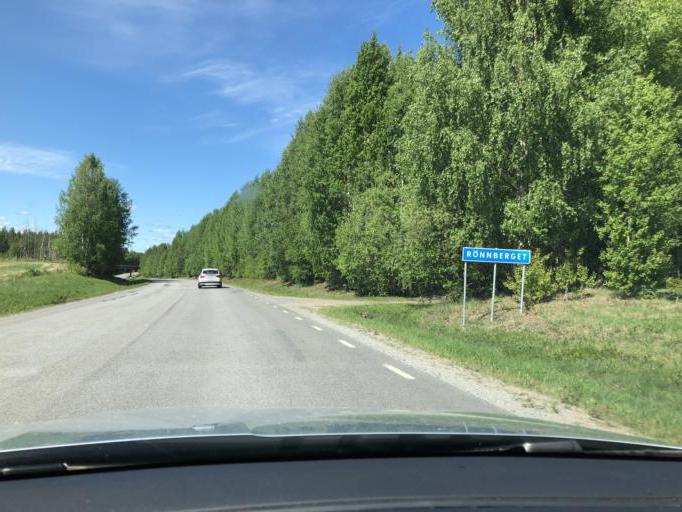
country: SE
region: Norrbotten
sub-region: Pitea Kommun
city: Roknas
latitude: 65.4451
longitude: 21.2570
